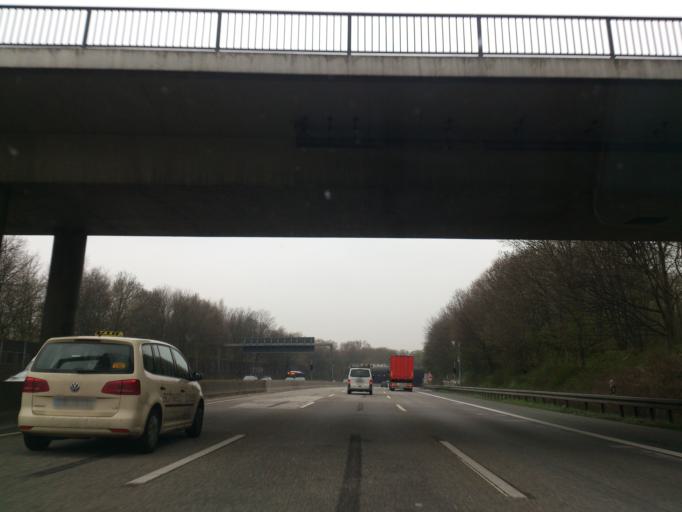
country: DE
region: North Rhine-Westphalia
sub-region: Regierungsbezirk Dusseldorf
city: Dusseldorf
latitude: 51.1903
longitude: 6.8302
